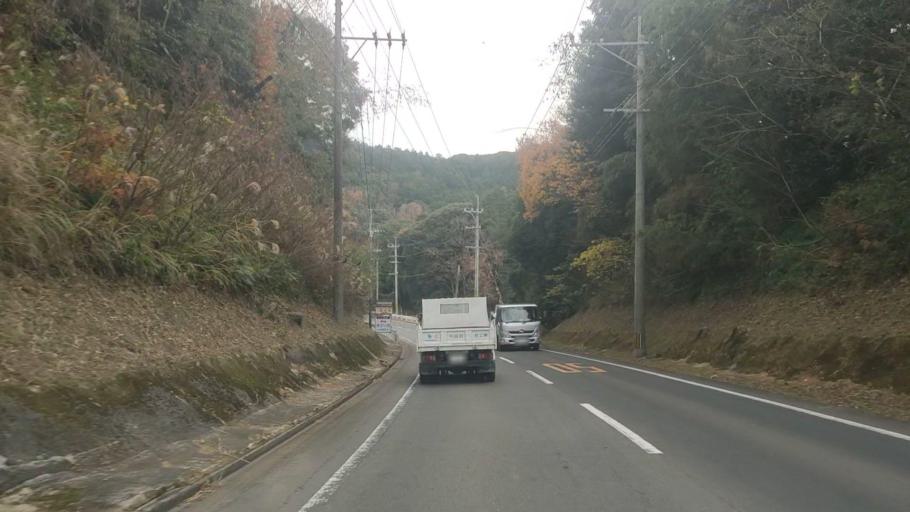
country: JP
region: Nagasaki
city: Shimabara
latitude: 32.8520
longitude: 130.2638
